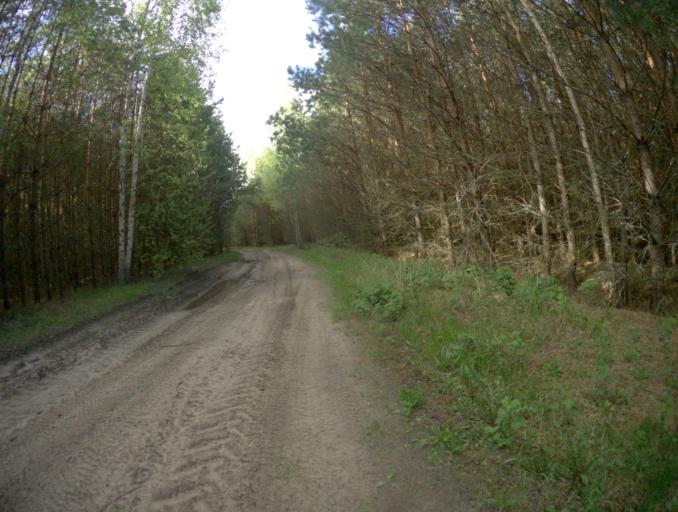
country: RU
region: Vladimir
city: Gusevskiy
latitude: 55.6102
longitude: 40.5427
